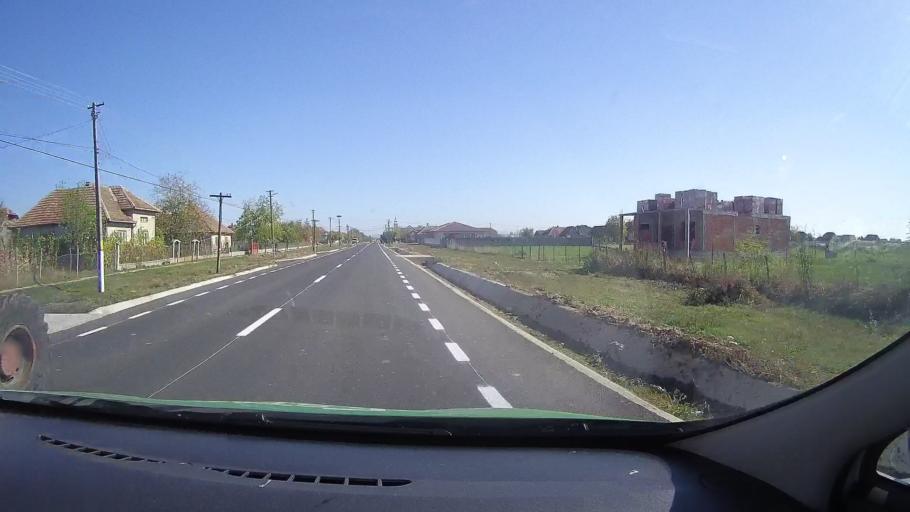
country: RO
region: Satu Mare
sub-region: Oras Ardud
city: Madaras
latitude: 47.6855
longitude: 22.8512
